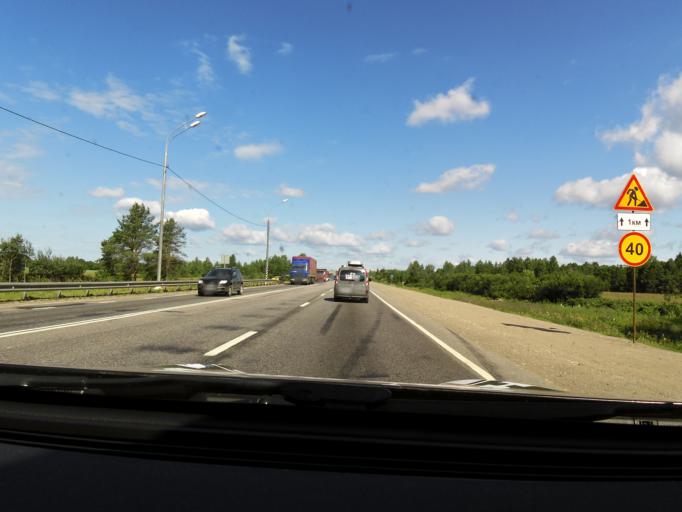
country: RU
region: Tverskaya
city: Tver
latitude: 56.8182
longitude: 35.8251
